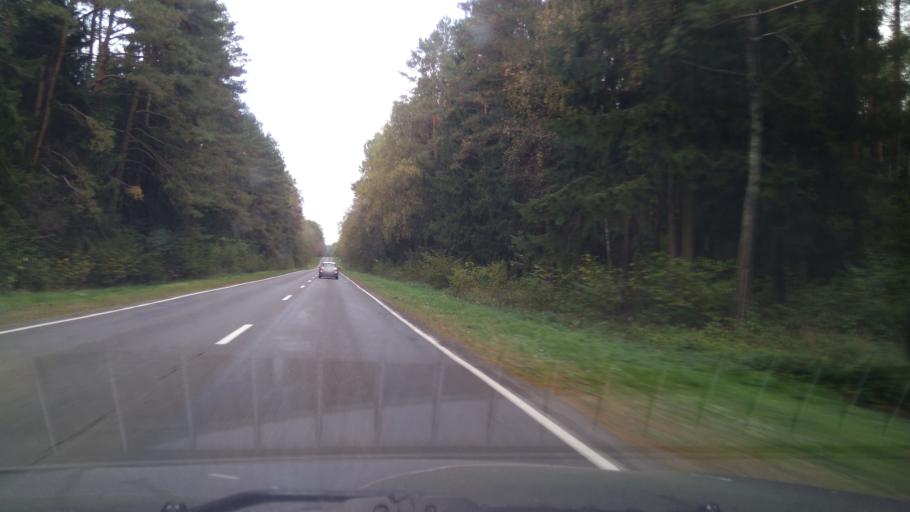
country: BY
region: Minsk
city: Druzhny
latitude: 53.6297
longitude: 27.8811
